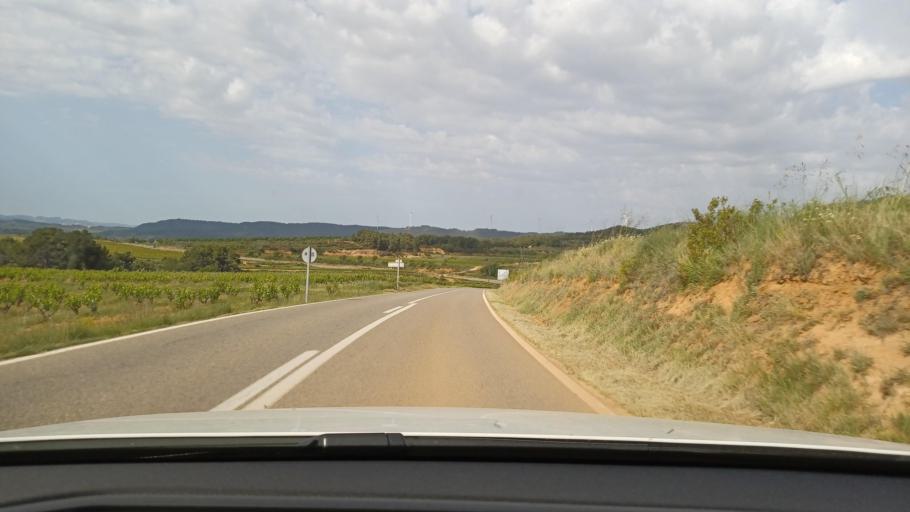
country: ES
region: Catalonia
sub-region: Provincia de Tarragona
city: Bot
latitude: 41.0386
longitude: 0.3829
